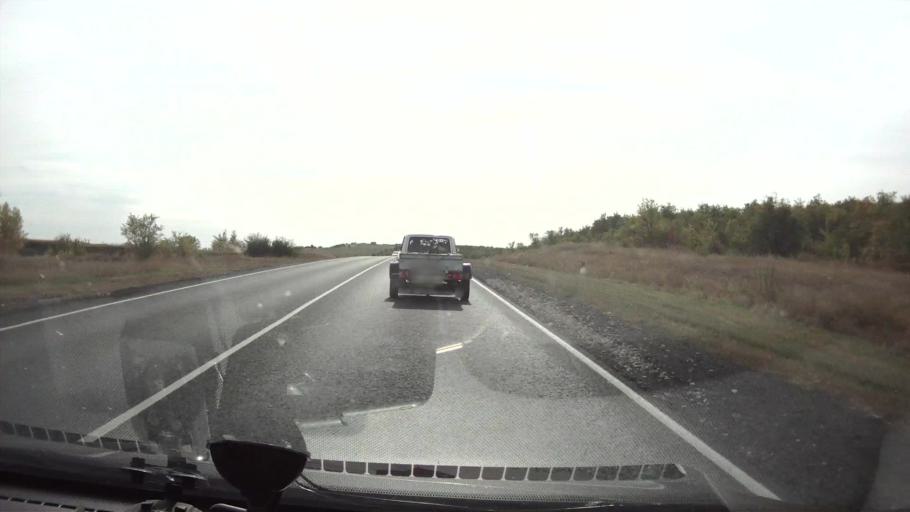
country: RU
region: Saratov
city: Balakovo
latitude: 52.1929
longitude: 47.8554
